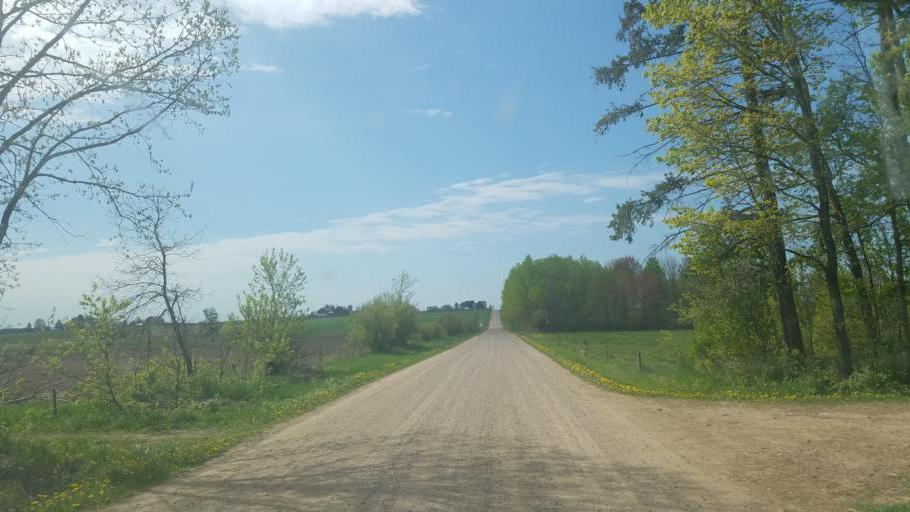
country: US
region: Wisconsin
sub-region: Marathon County
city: Spencer
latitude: 44.6064
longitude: -90.3766
